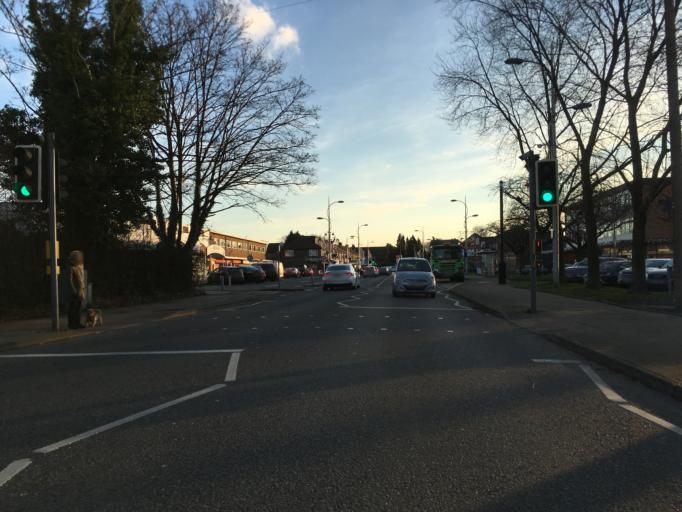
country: GB
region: England
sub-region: Cheshire East
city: Wilmslow
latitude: 53.3505
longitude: -2.2155
